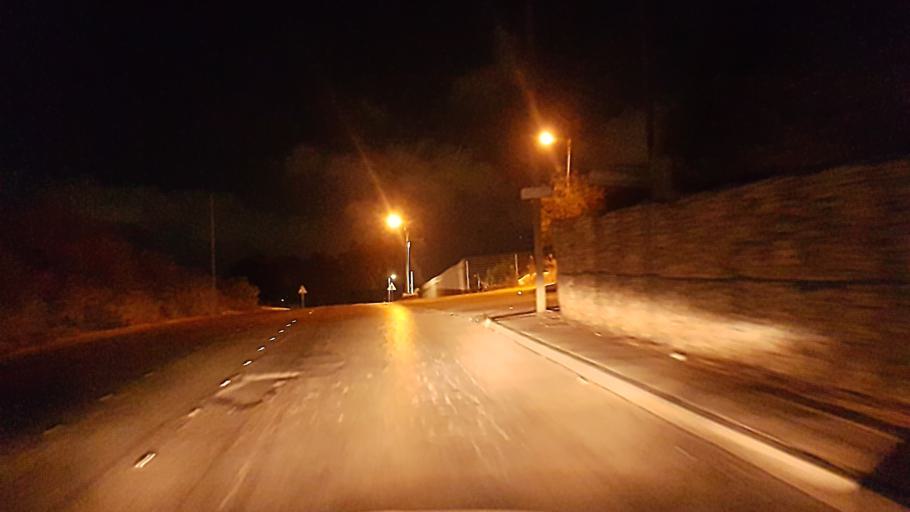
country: IL
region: Central District
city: Hod HaSharon
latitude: 32.1624
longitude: 34.8771
